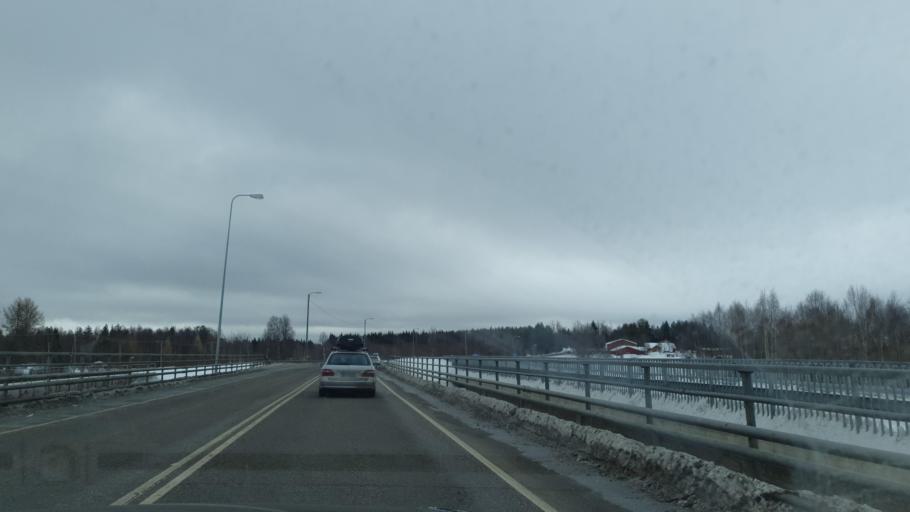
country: FI
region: Lapland
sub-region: Kemi-Tornio
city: Tornio
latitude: 66.0125
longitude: 24.0685
